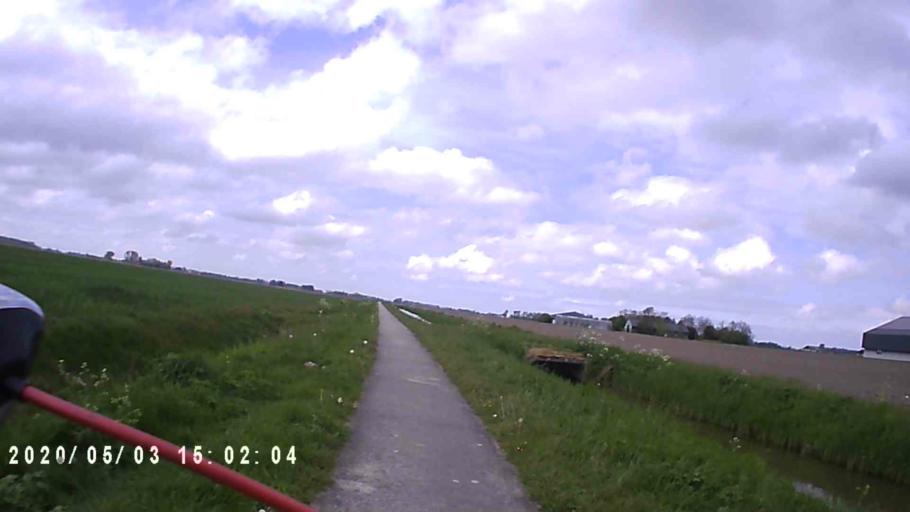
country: NL
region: Groningen
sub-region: Gemeente Zuidhorn
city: Oldehove
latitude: 53.3621
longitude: 6.4450
